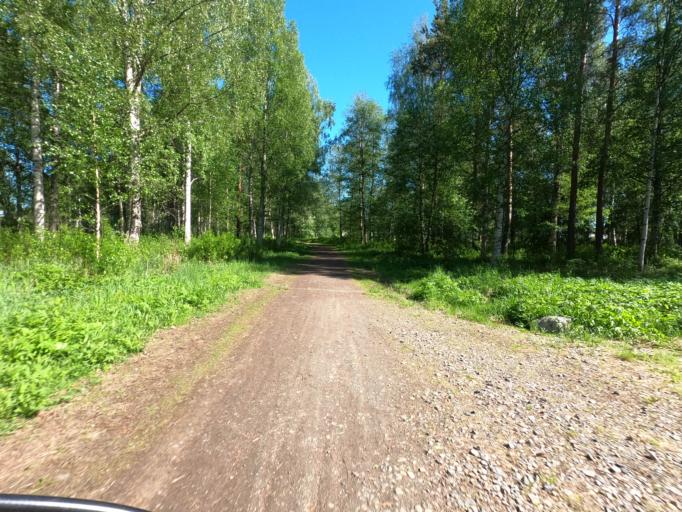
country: FI
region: North Karelia
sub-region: Joensuu
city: Joensuu
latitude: 62.6052
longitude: 29.8118
